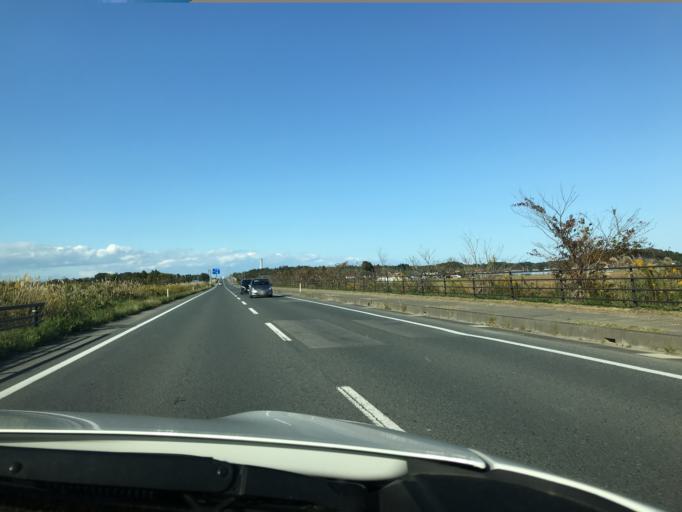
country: JP
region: Miyagi
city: Marumori
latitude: 37.7966
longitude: 140.9438
